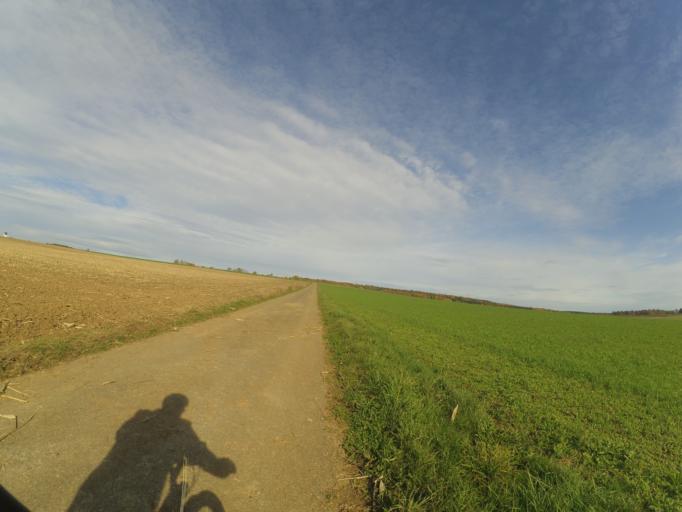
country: DE
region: Baden-Wuerttemberg
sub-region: Tuebingen Region
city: Lonsee
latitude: 48.5787
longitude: 9.9265
